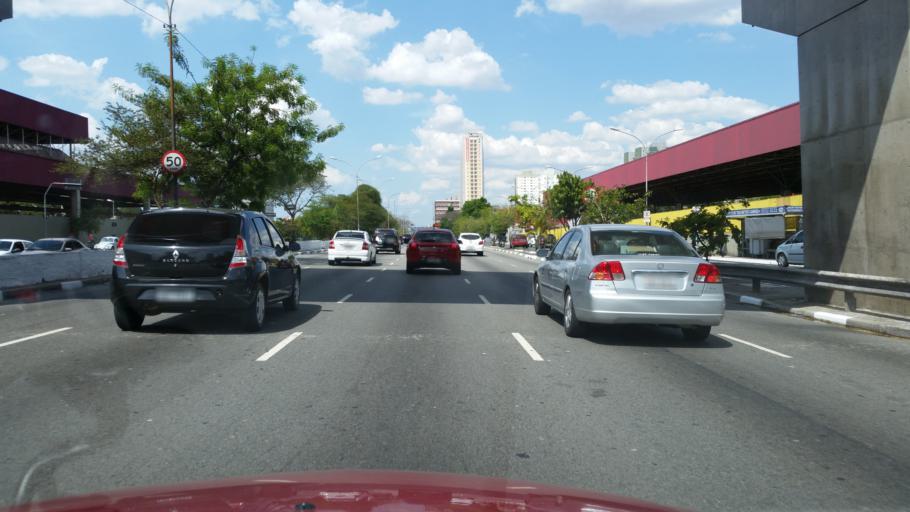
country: BR
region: Sao Paulo
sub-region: Sao Paulo
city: Sao Paulo
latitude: -23.5384
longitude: -46.5648
